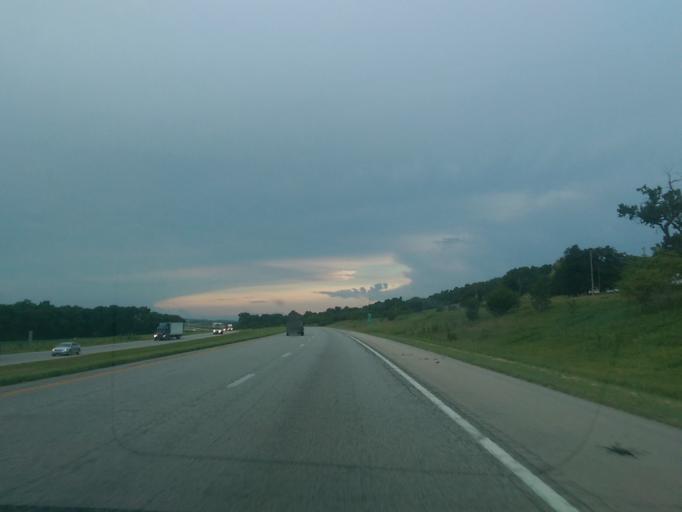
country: US
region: Missouri
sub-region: Holt County
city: Mound City
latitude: 40.1065
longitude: -95.2160
